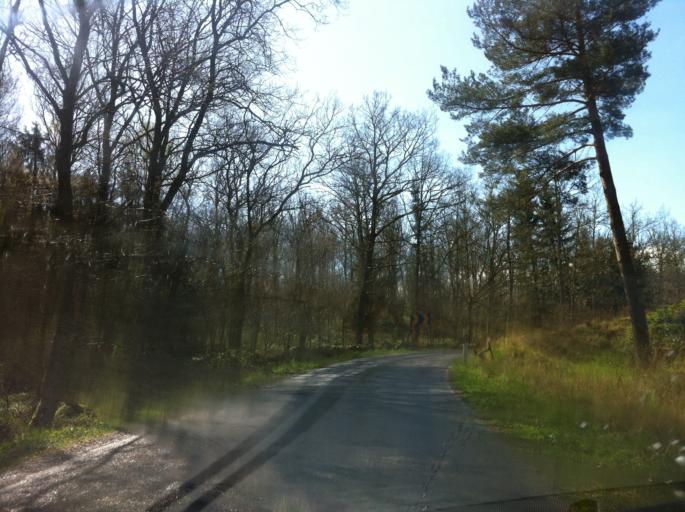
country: SE
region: Skane
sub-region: Hoors Kommun
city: Satofta
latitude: 55.9112
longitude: 13.6119
